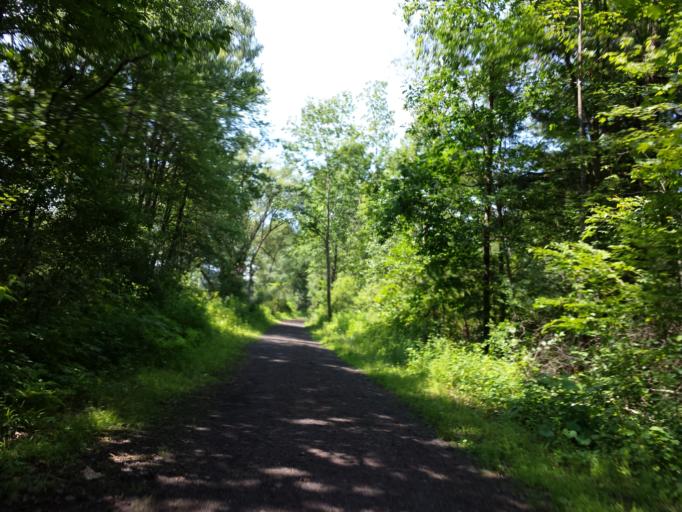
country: US
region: Vermont
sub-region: Rutland County
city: Castleton
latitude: 43.6001
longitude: -73.1835
